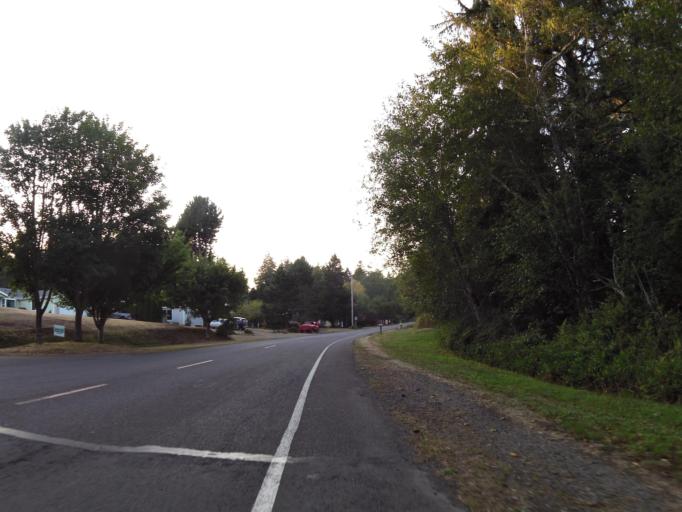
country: US
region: Oregon
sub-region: Clatsop County
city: Warrenton
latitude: 46.1583
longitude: -123.9439
